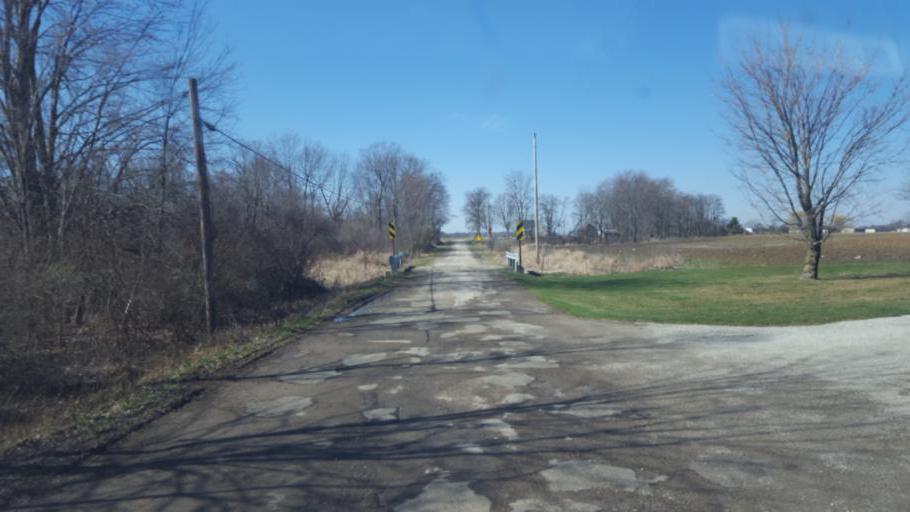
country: US
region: Ohio
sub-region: Morrow County
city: Cardington
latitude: 40.4851
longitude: -82.9676
